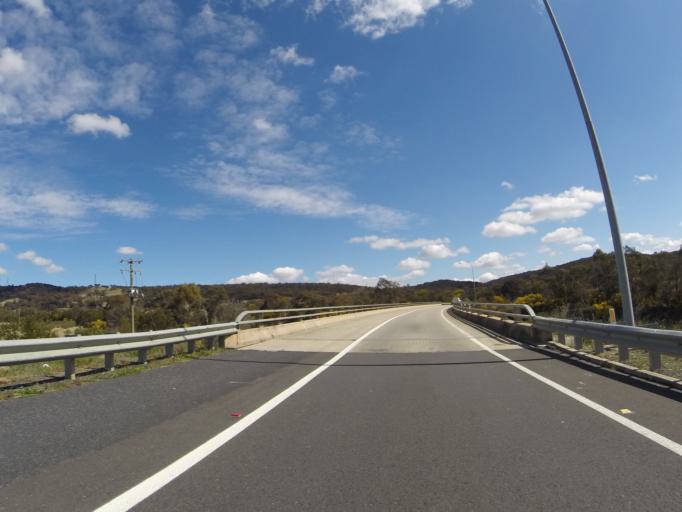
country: AU
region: New South Wales
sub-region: Goulburn Mulwaree
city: Goulburn
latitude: -34.7424
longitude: 149.7732
